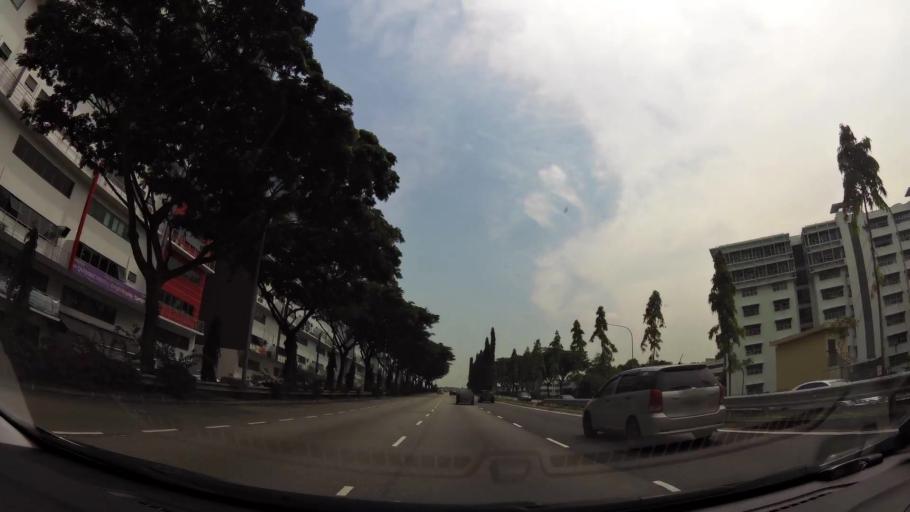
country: SG
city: Singapore
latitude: 1.3382
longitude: 103.9048
